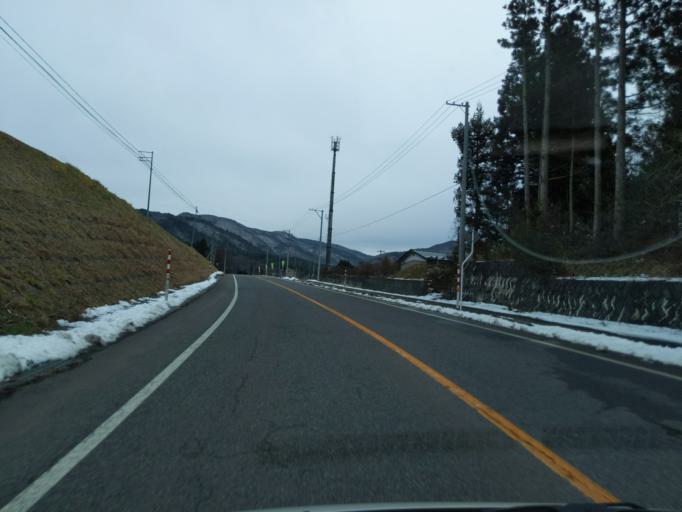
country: JP
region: Iwate
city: Mizusawa
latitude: 39.1171
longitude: 141.2588
